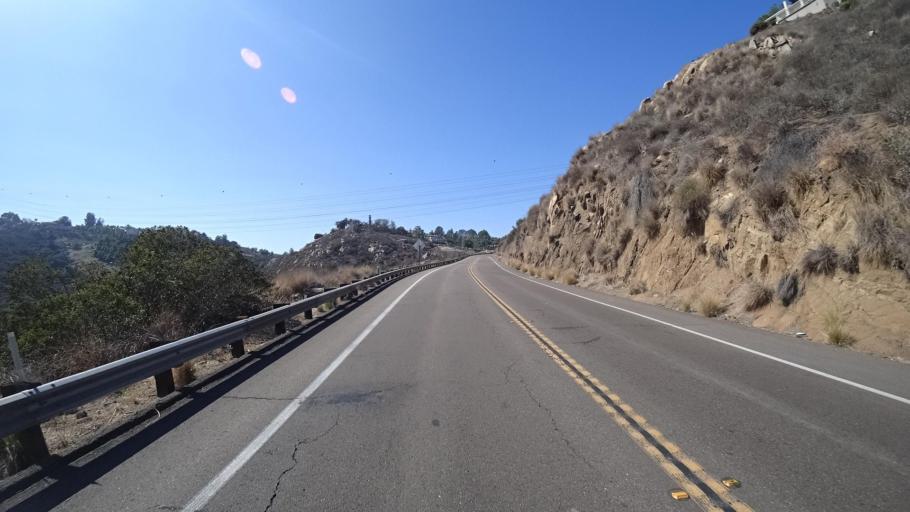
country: US
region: California
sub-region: San Diego County
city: Granite Hills
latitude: 32.7851
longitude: -116.8907
